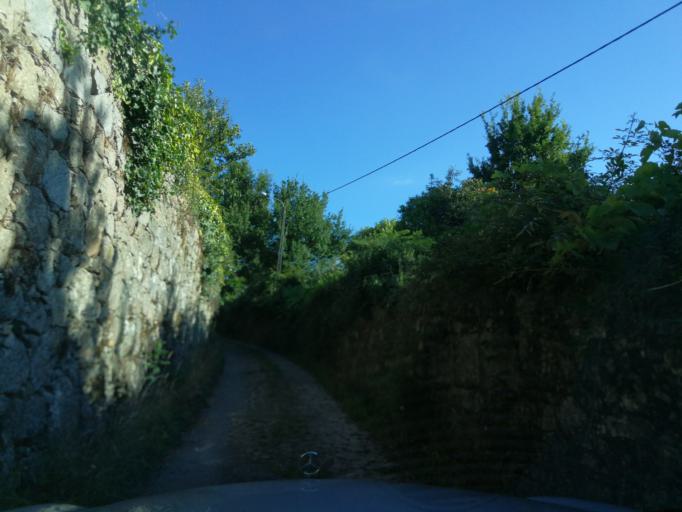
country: PT
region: Braga
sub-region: Braga
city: Braga
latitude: 41.5481
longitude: -8.3945
